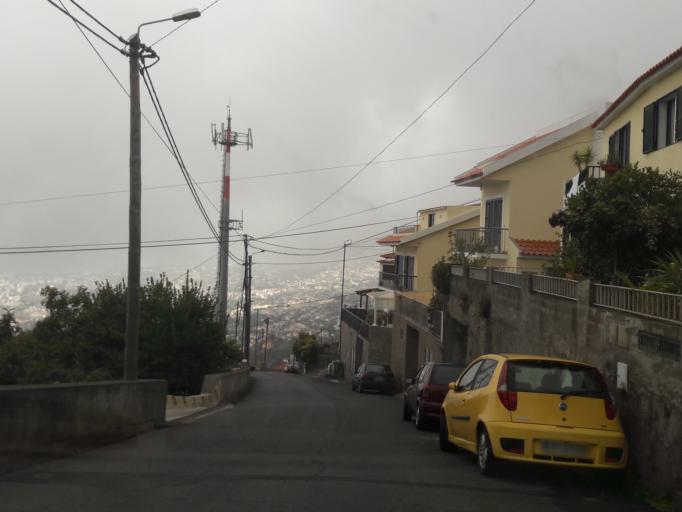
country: PT
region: Madeira
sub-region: Funchal
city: Nossa Senhora do Monte
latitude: 32.6665
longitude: -16.8910
